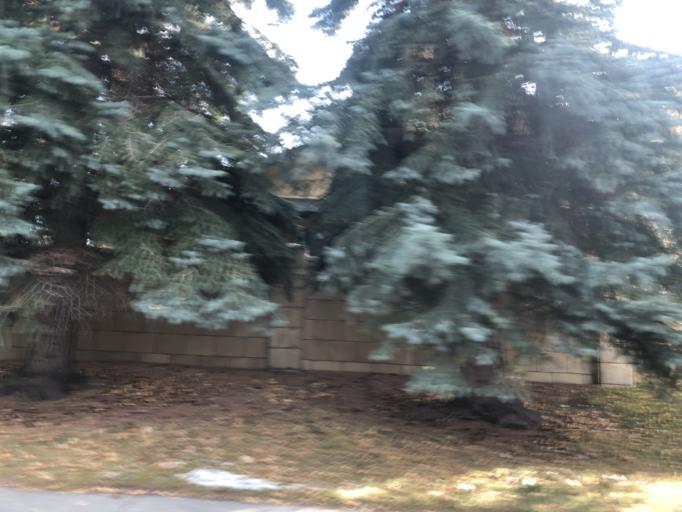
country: CA
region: Alberta
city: Calgary
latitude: 50.9344
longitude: -114.0595
